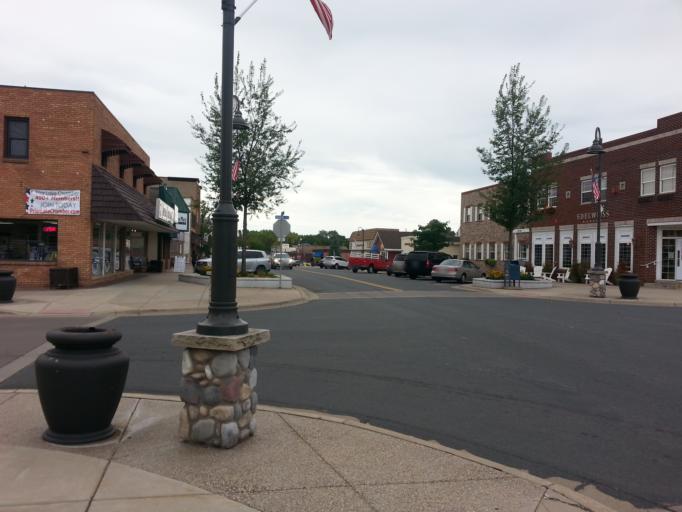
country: US
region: Minnesota
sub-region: Scott County
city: Prior Lake
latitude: 44.7149
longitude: -93.4238
